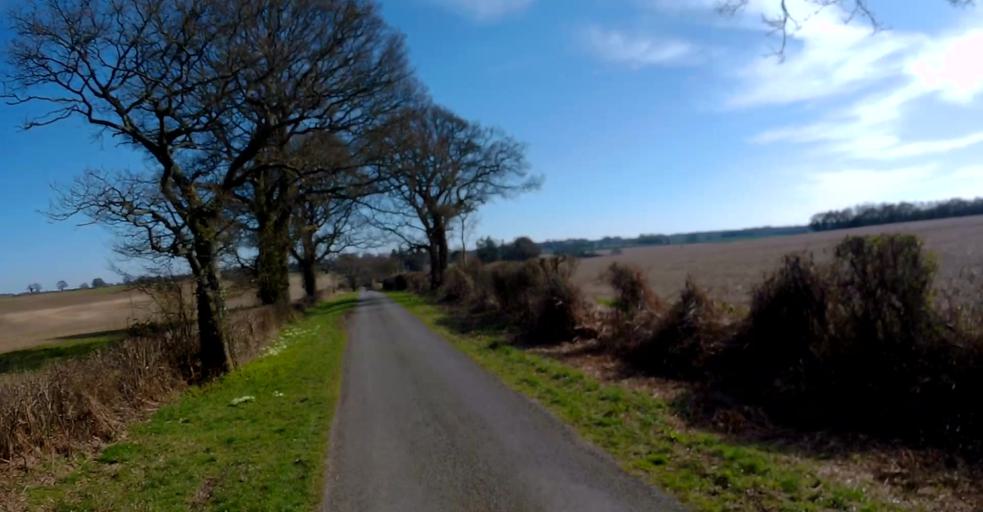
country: GB
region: England
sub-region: Hampshire
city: Four Marks
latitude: 51.1688
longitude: -1.0637
